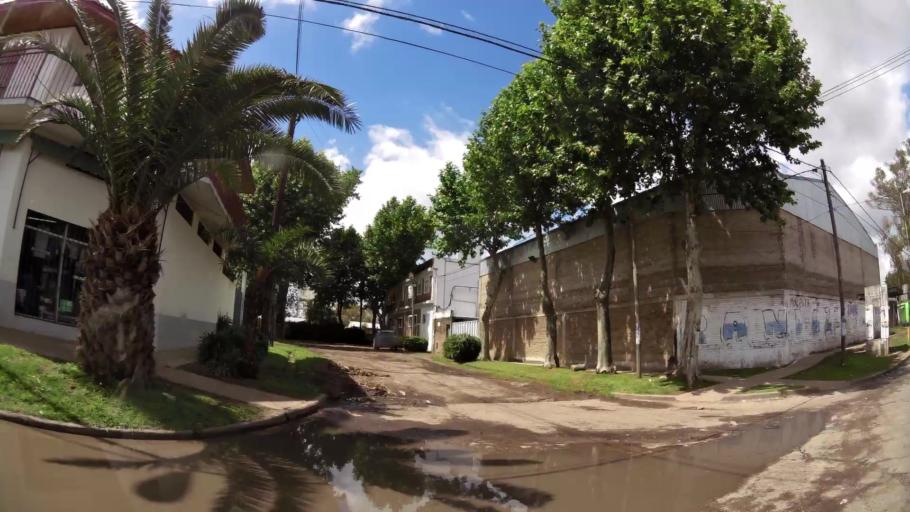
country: AR
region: Buenos Aires
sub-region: Partido de Quilmes
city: Quilmes
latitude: -34.8288
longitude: -58.2157
